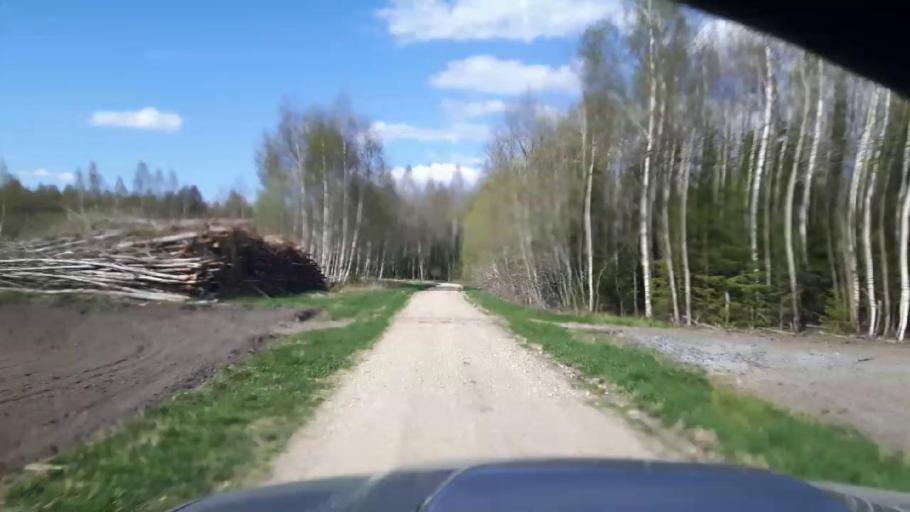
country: EE
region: Paernumaa
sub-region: Tootsi vald
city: Tootsi
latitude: 58.4559
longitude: 24.8461
